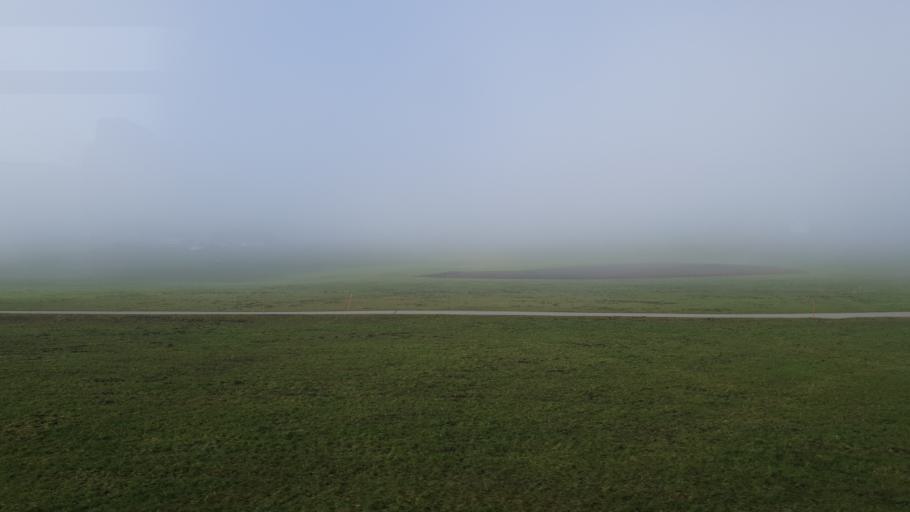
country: CH
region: Fribourg
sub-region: Gruyere District
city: Sales
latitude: 46.5988
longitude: 6.9363
